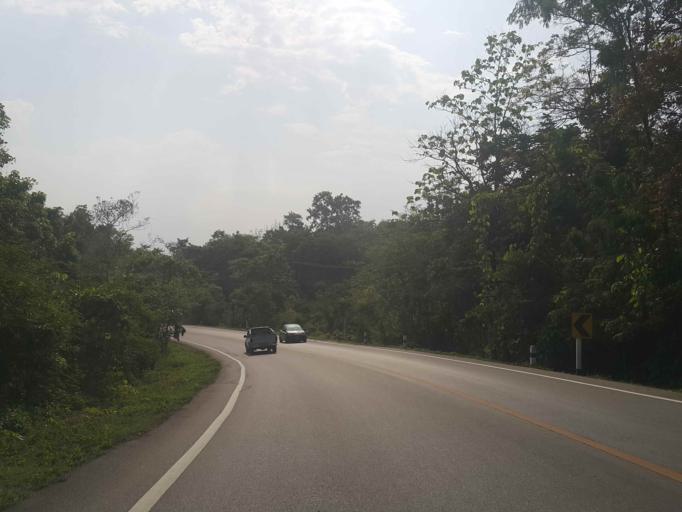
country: TH
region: Chiang Mai
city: Mae Taeng
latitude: 19.0708
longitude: 98.9746
